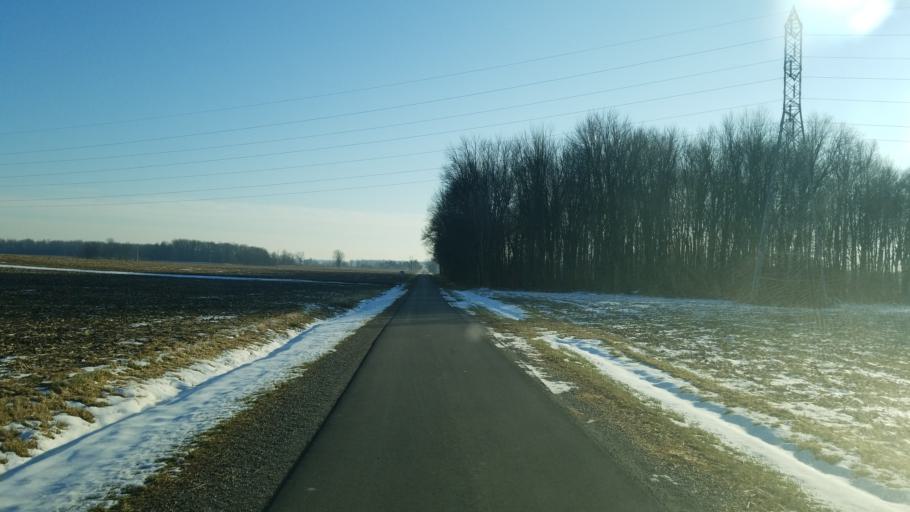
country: US
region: Ohio
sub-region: Crawford County
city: Bucyrus
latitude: 40.9573
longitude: -82.9207
